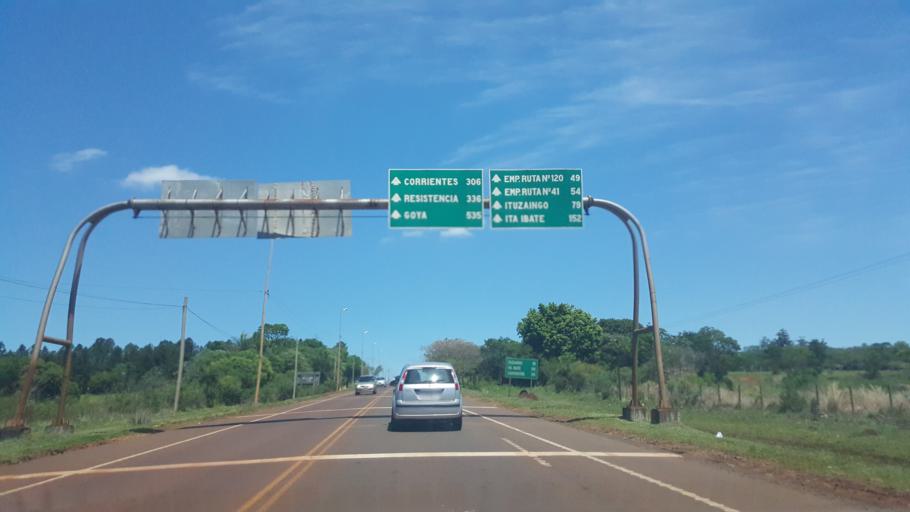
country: AR
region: Misiones
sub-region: Departamento de Capital
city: Posadas
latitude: -27.4026
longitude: -55.9678
